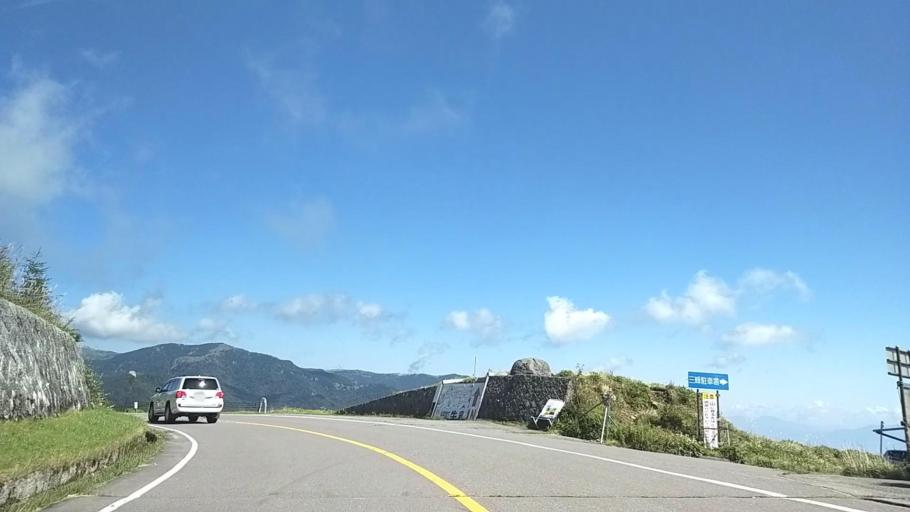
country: JP
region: Nagano
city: Suwa
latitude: 36.1639
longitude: 138.1365
